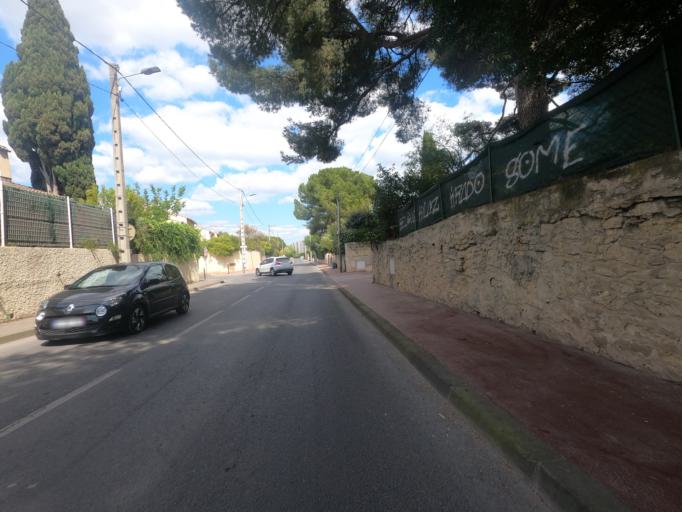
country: FR
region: Languedoc-Roussillon
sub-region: Departement de l'Herault
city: Montpellier
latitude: 43.5891
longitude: 3.8704
